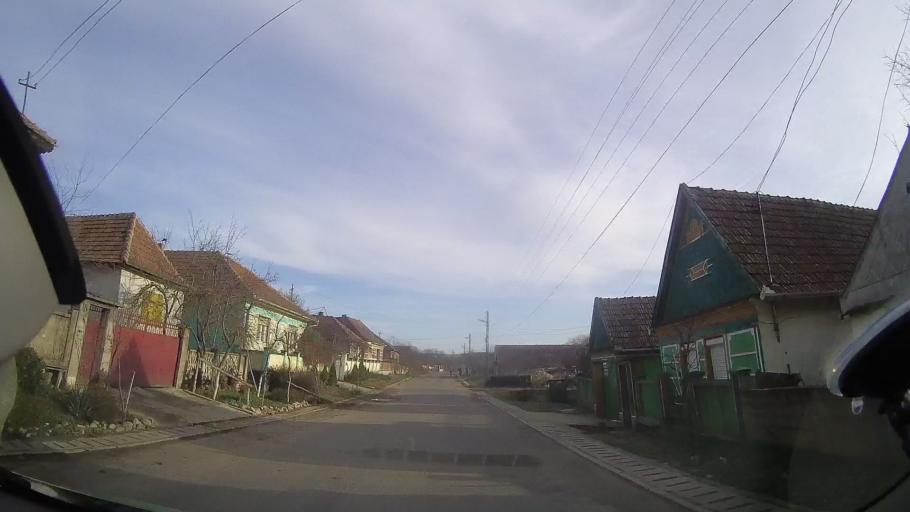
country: RO
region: Bihor
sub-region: Comuna Sarbi
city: Burzuc
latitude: 47.1478
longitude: 22.1784
